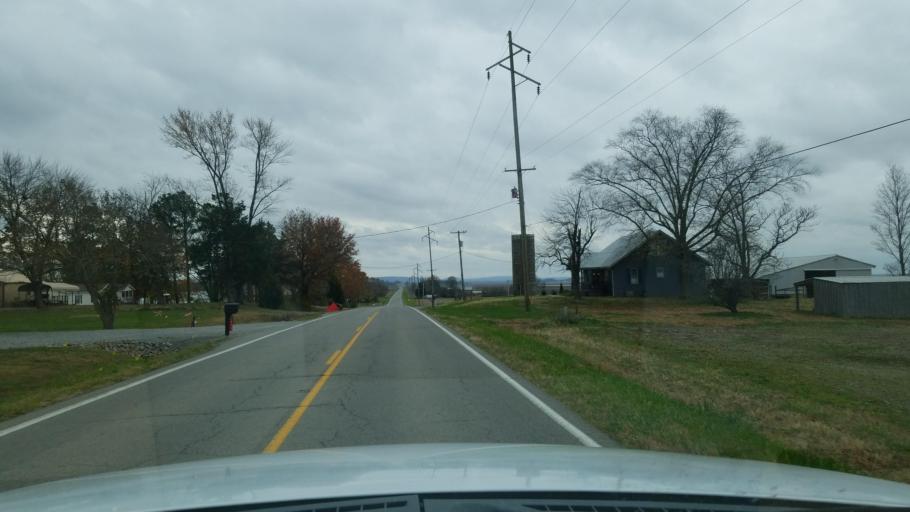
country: US
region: Illinois
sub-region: Saline County
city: Eldorado
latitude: 37.7927
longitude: -88.4382
